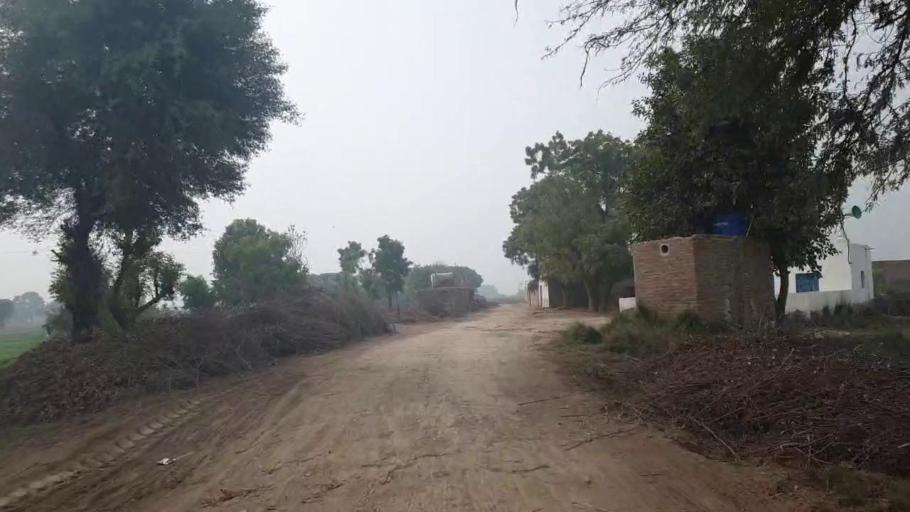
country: PK
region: Sindh
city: Tando Adam
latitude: 25.7182
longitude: 68.6233
